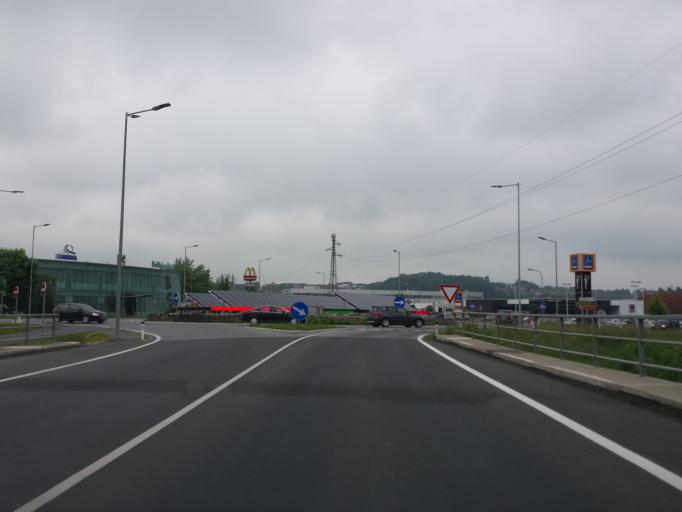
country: AT
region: Styria
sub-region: Politischer Bezirk Weiz
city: Krottendorf
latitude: 47.2055
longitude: 15.6373
